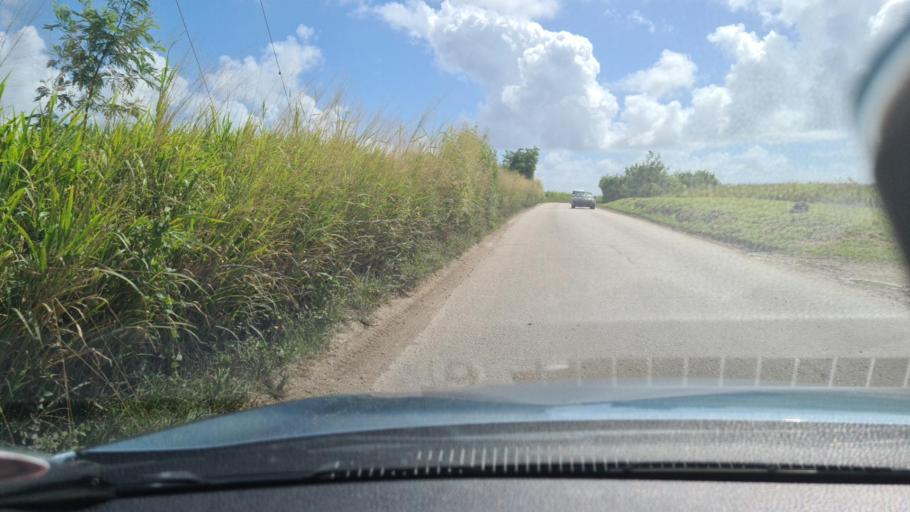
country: BB
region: Christ Church
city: Oistins
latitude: 13.0965
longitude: -59.5228
